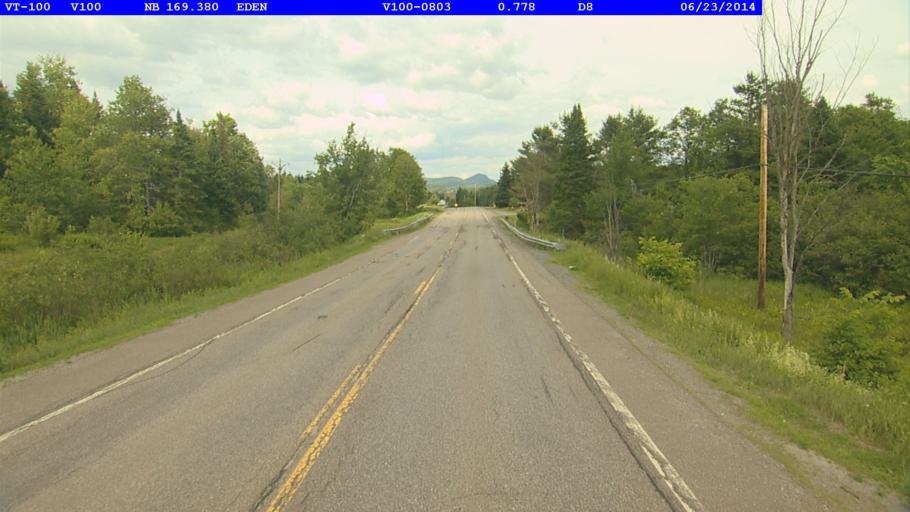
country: US
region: Vermont
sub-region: Lamoille County
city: Hyde Park
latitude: 44.6933
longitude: -72.5830
